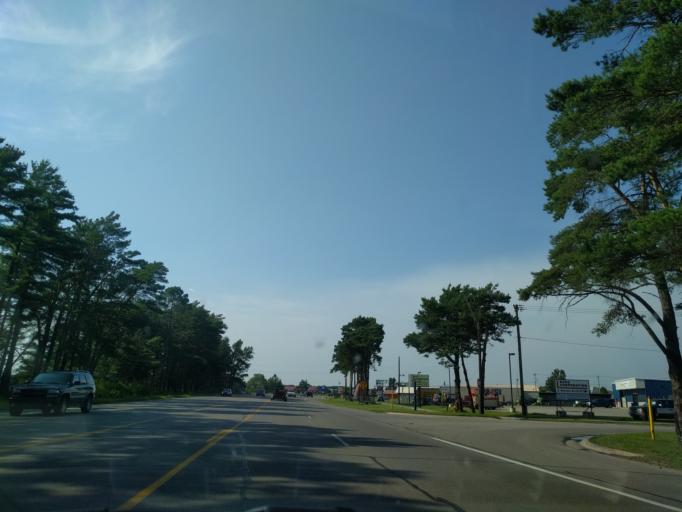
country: US
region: Michigan
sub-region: Delta County
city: Escanaba
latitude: 45.7713
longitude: -87.0816
